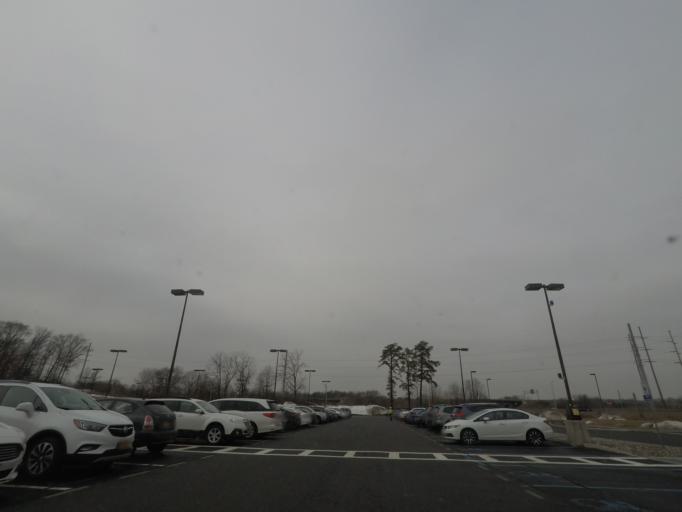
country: US
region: New York
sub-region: Albany County
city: McKownville
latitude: 42.6916
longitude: -73.8364
